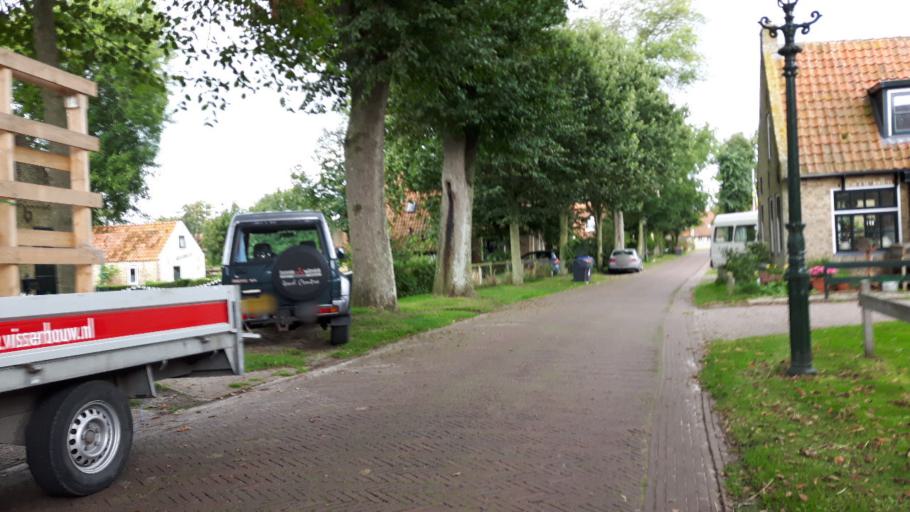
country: NL
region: Friesland
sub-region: Gemeente Ameland
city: Hollum
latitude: 53.4370
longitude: 5.6414
